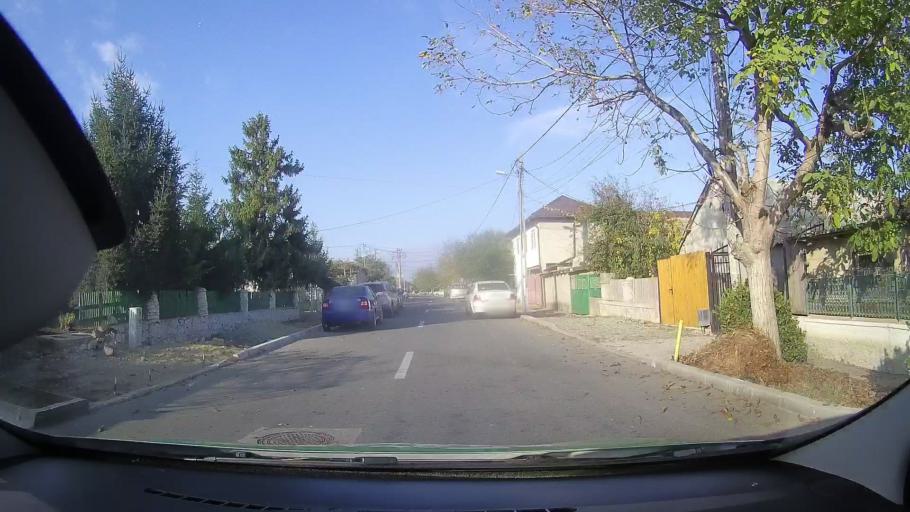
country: RO
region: Constanta
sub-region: Comuna Lumina
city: Lumina
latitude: 44.2868
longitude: 28.5648
